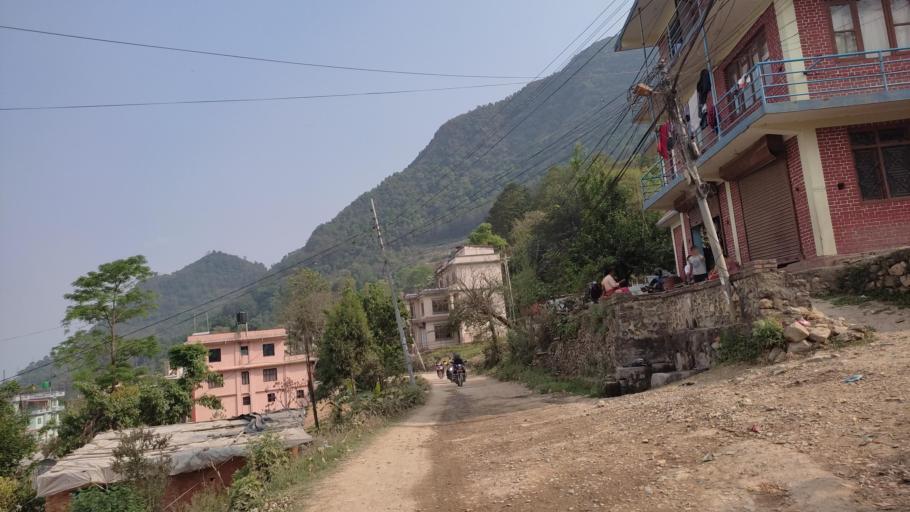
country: NP
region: Central Region
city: Kirtipur
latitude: 27.6628
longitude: 85.2582
